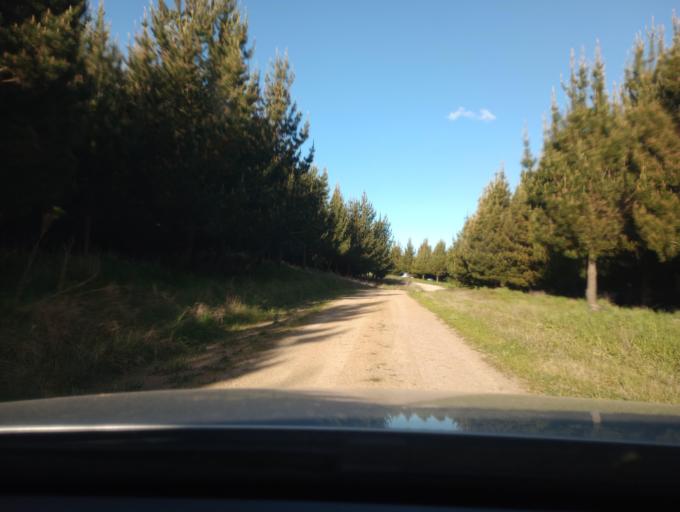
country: AU
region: New South Wales
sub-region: Blayney
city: Millthorpe
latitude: -33.3979
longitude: 149.3125
